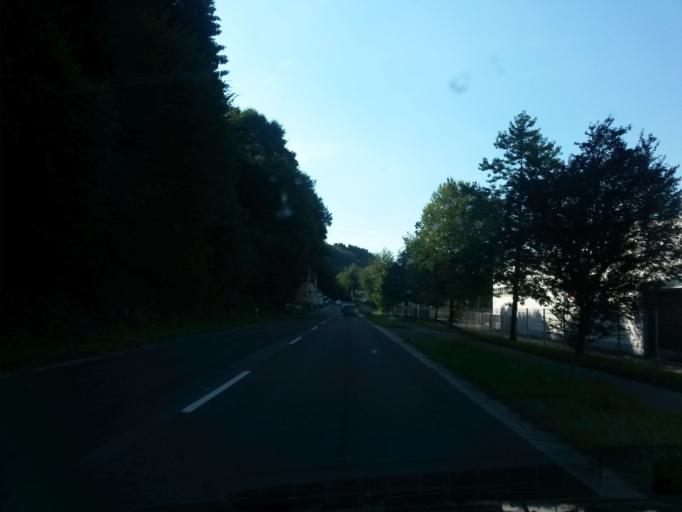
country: DE
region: North Rhine-Westphalia
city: Wiehl
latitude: 50.9793
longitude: 7.4852
